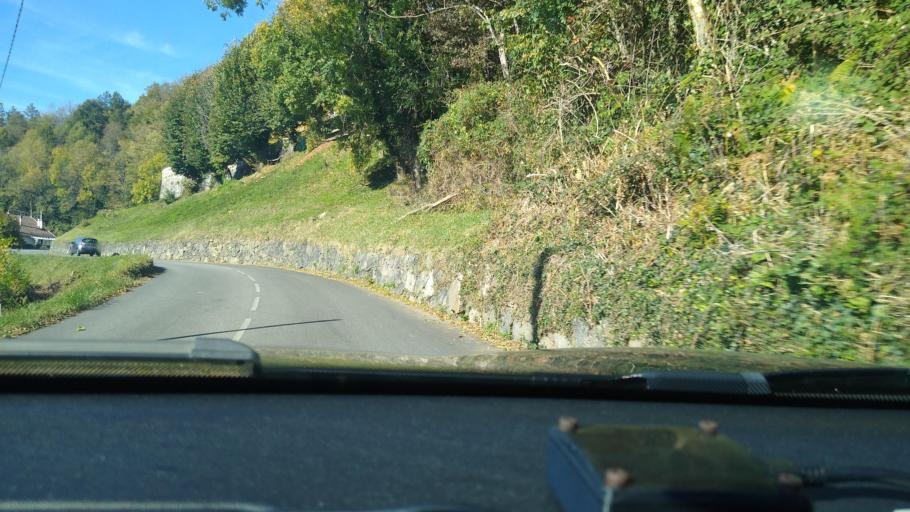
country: FR
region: Midi-Pyrenees
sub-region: Departement de l'Ariege
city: Ax-les-Thermes
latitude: 42.7220
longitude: 1.8450
